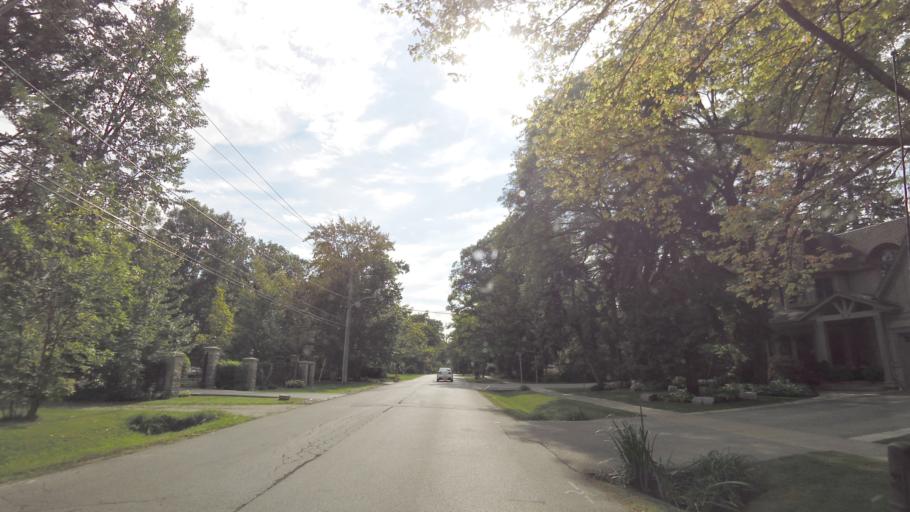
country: CA
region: Ontario
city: Mississauga
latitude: 43.5599
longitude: -79.5926
